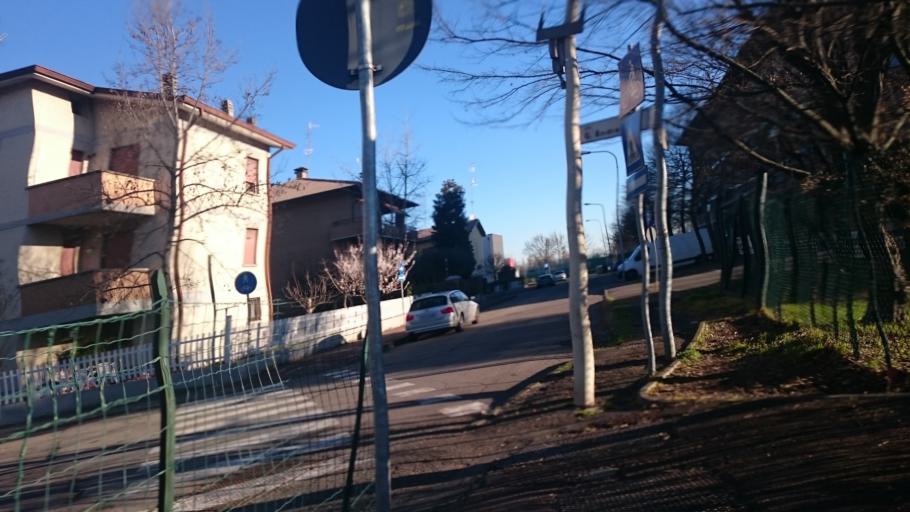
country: IT
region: Emilia-Romagna
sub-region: Provincia di Reggio Emilia
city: Reggio nell'Emilia
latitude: 44.7118
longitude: 10.6362
